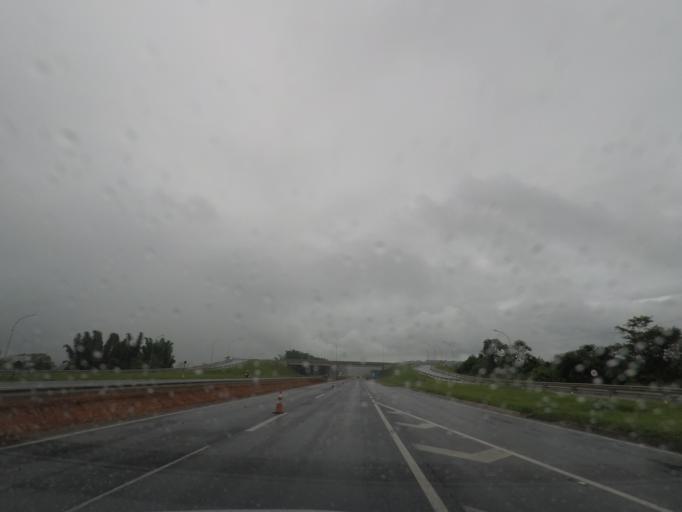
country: BR
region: Sao Paulo
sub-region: Jacupiranga
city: Jacupiranga
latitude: -24.6880
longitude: -47.9907
